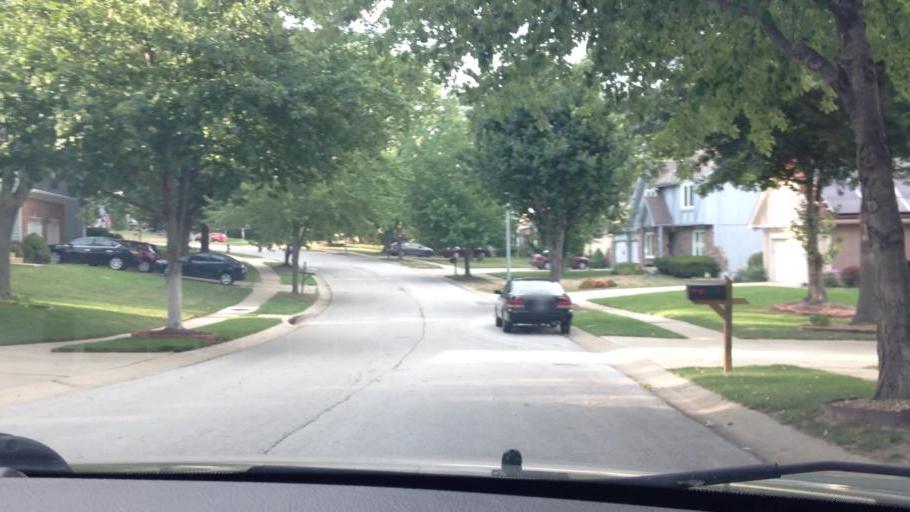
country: US
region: Missouri
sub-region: Platte County
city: Riverside
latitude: 39.2145
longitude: -94.6354
